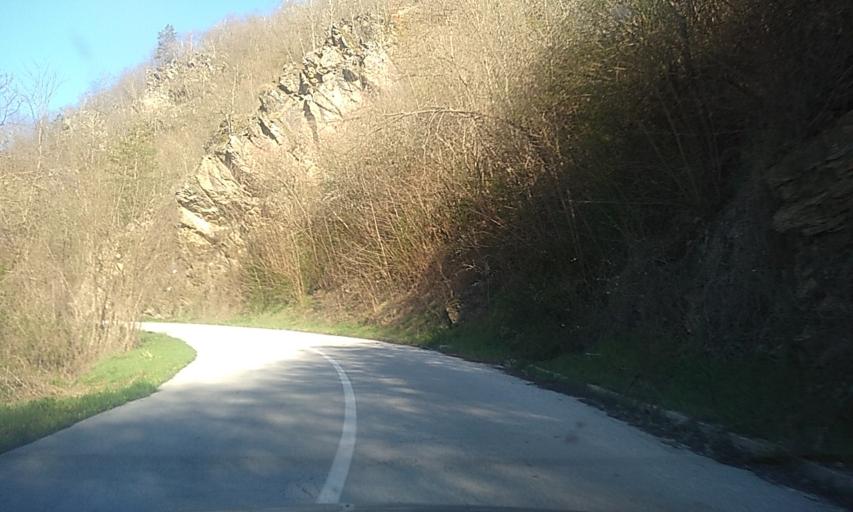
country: RS
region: Central Serbia
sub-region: Pcinjski Okrug
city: Bosilegrad
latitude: 42.4170
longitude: 22.5210
